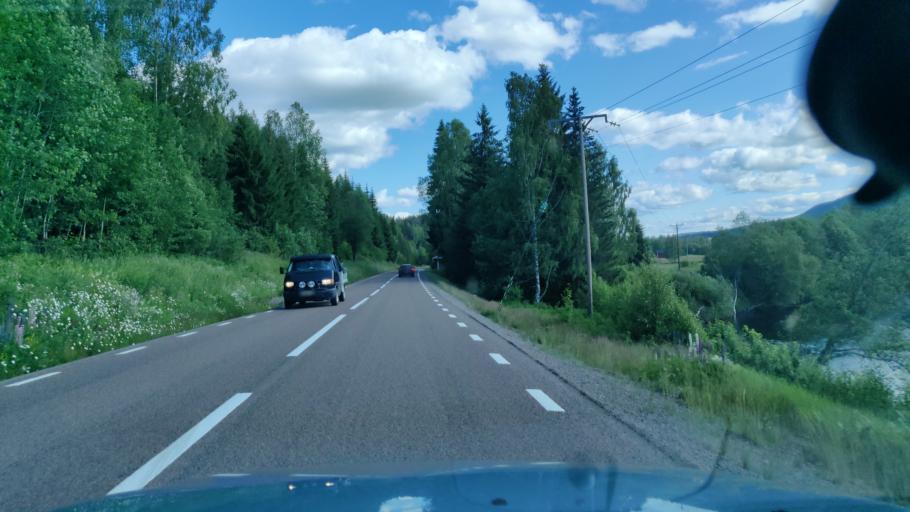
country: SE
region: Vaermland
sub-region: Torsby Kommun
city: Torsby
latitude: 60.6383
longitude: 13.0130
